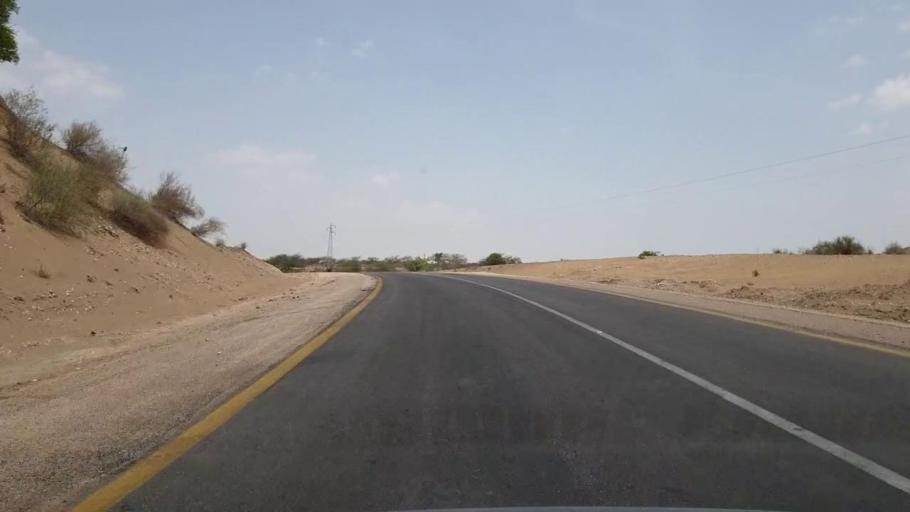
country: PK
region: Sindh
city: Mithi
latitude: 24.7967
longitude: 69.7452
